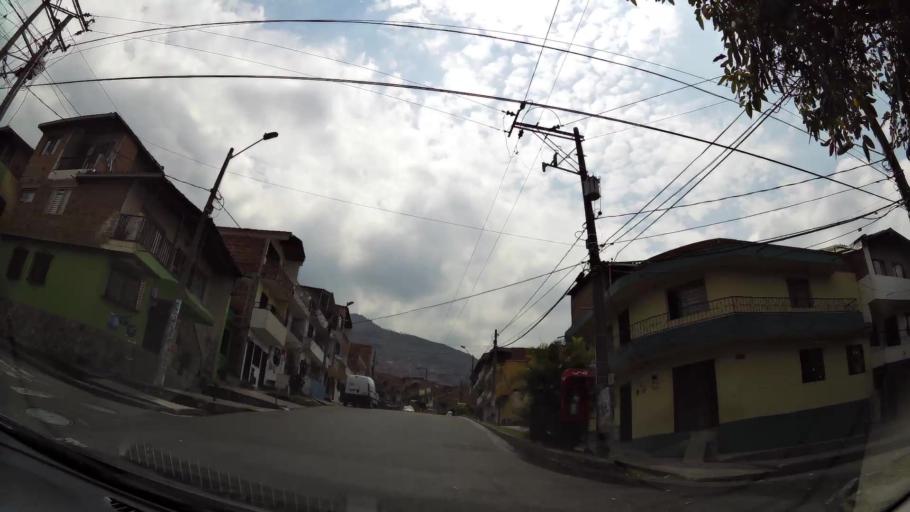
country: CO
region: Antioquia
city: Medellin
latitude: 6.2688
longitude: -75.5521
